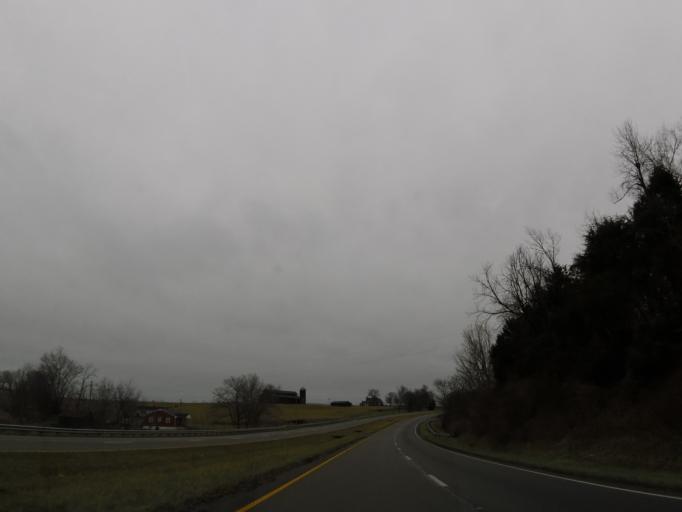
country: US
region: Kentucky
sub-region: Lincoln County
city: Stanford
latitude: 37.5595
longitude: -84.6776
